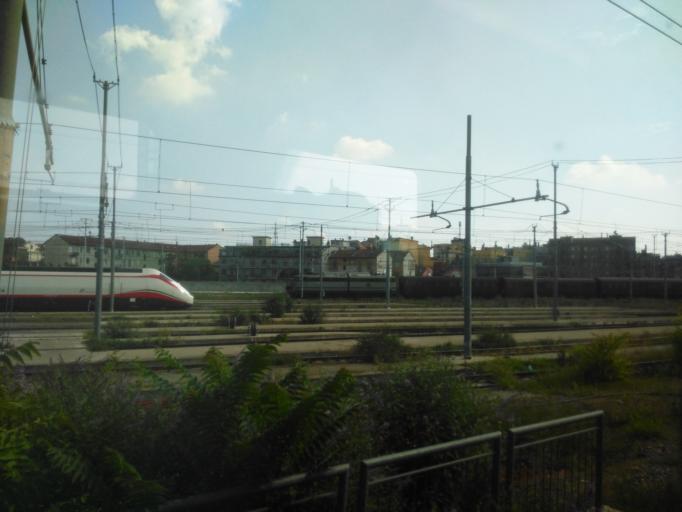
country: IT
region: Lombardy
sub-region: Citta metropolitana di Milano
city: Sesto San Giovanni
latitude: 45.4975
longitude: 9.2153
